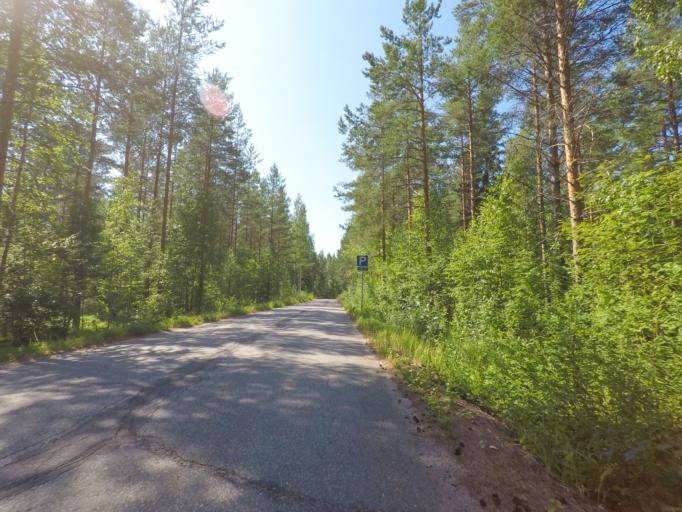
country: FI
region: Southern Savonia
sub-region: Mikkeli
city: Puumala
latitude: 61.4070
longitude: 28.0851
